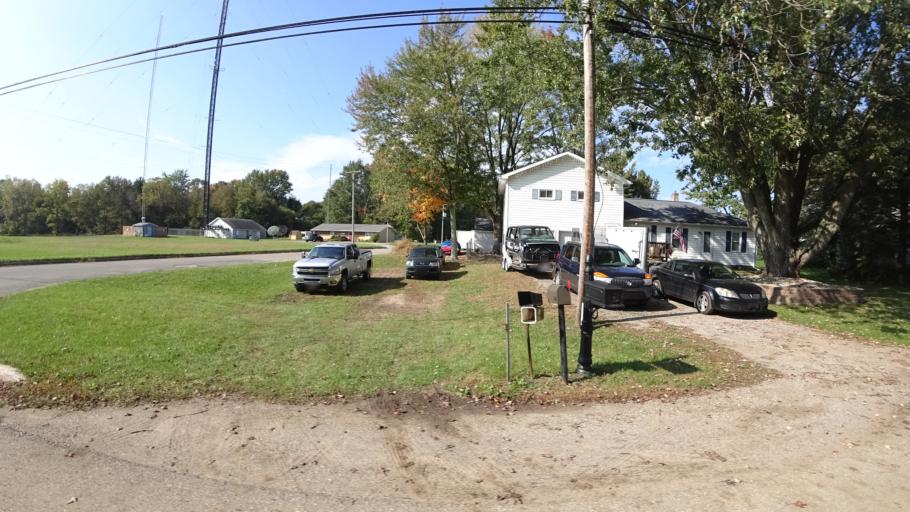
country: US
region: Michigan
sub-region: Saint Joseph County
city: Three Rivers
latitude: 41.9293
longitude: -85.6368
